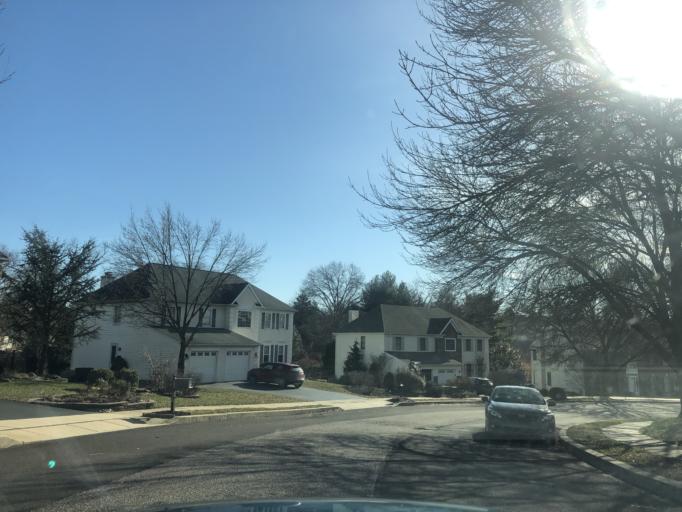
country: US
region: Pennsylvania
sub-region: Montgomery County
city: Plymouth Meeting
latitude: 40.0853
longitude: -75.2586
